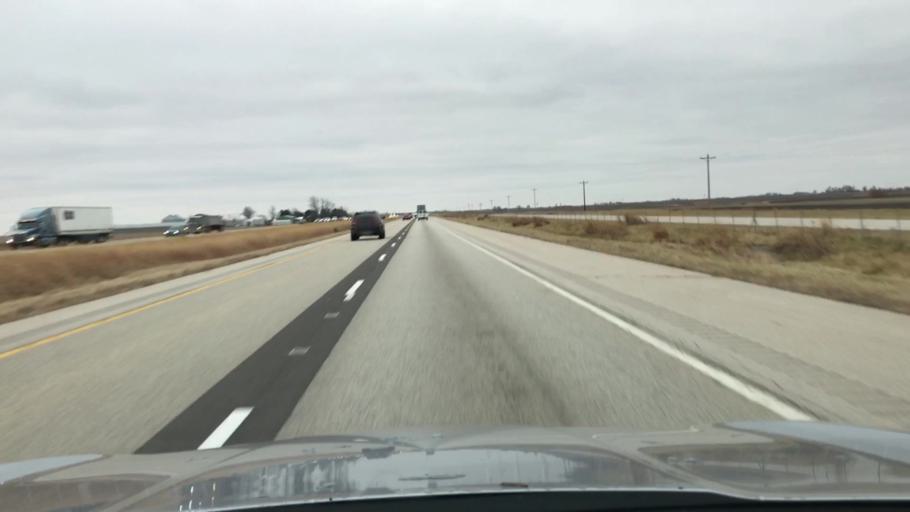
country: US
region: Illinois
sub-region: Sangamon County
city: Divernon
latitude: 39.4974
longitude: -89.6454
